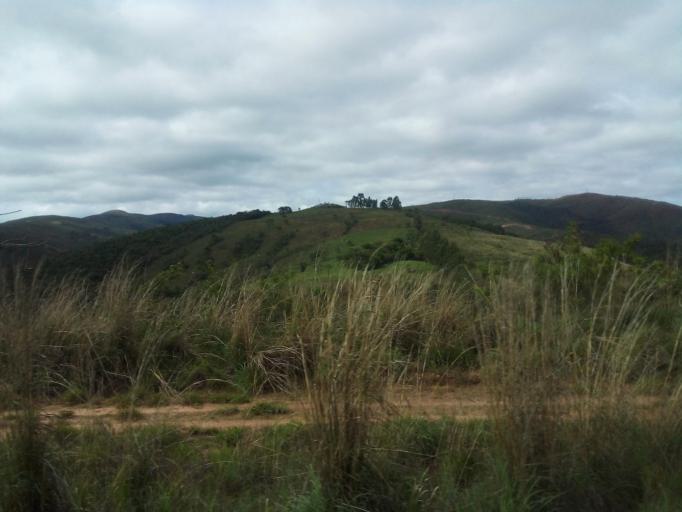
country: BR
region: Minas Gerais
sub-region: Caete
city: Caete
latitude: -19.9061
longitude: -43.7204
